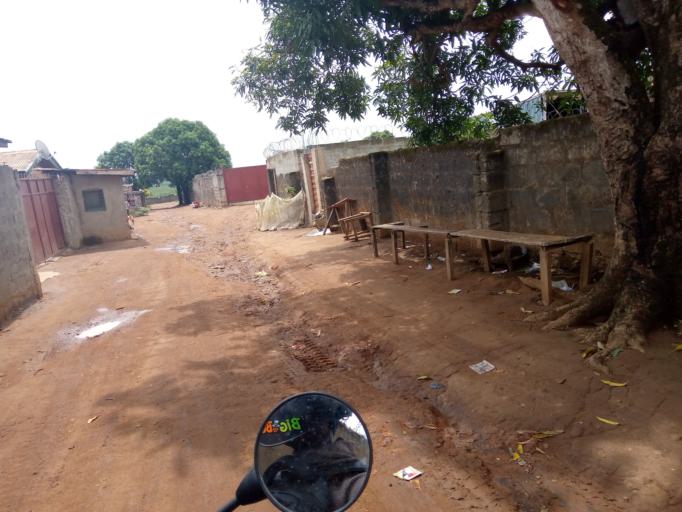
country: SL
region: Western Area
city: Hastings
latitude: 8.4131
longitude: -13.1423
